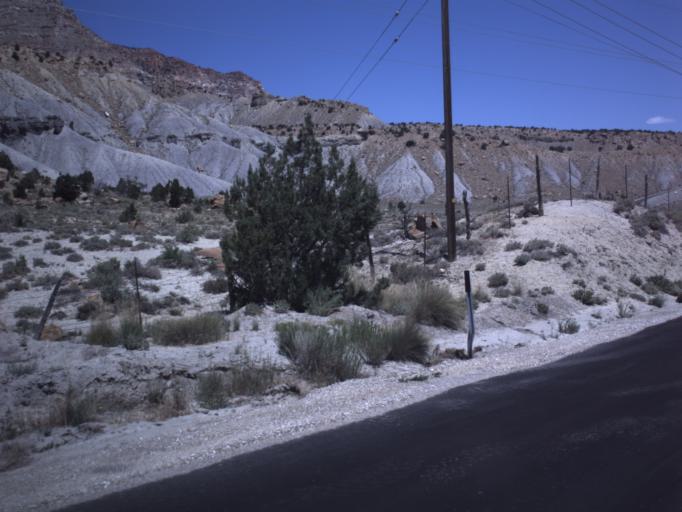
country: US
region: Utah
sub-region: Emery County
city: Orangeville
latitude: 39.2746
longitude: -111.1617
